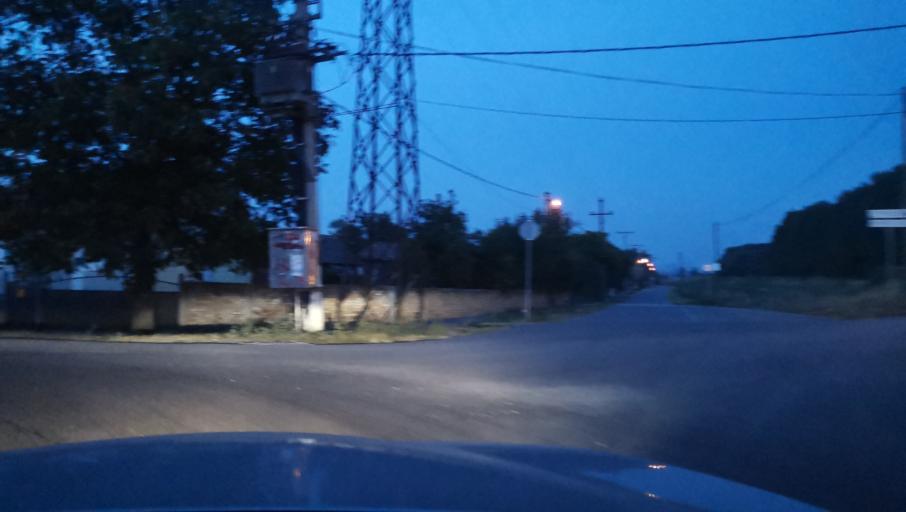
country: RS
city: Boljevci
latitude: 44.7185
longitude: 20.2231
